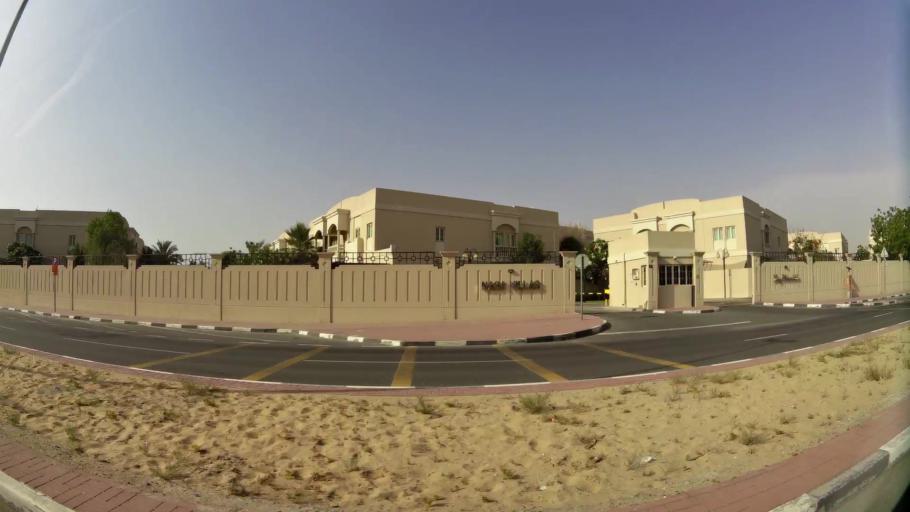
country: AE
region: Ash Shariqah
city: Sharjah
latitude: 25.2387
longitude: 55.3481
